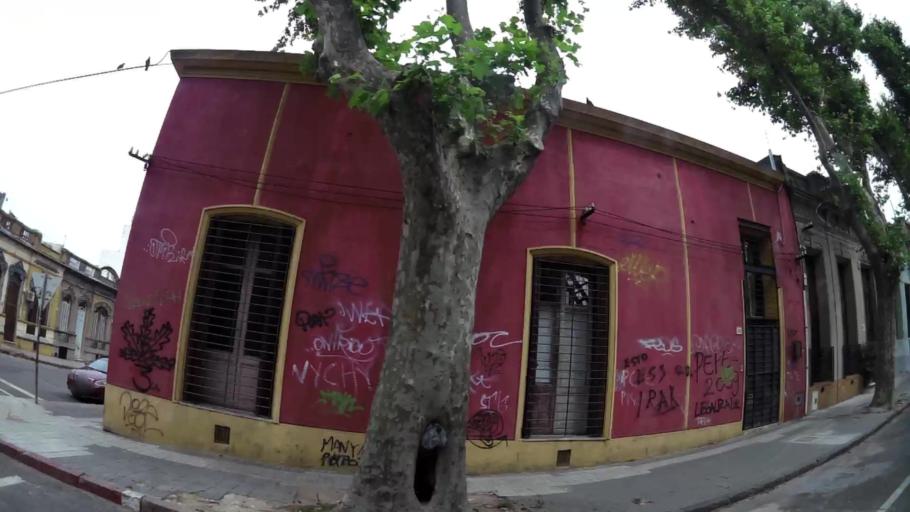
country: UY
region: Montevideo
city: Montevideo
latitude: -34.9095
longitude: -56.1729
